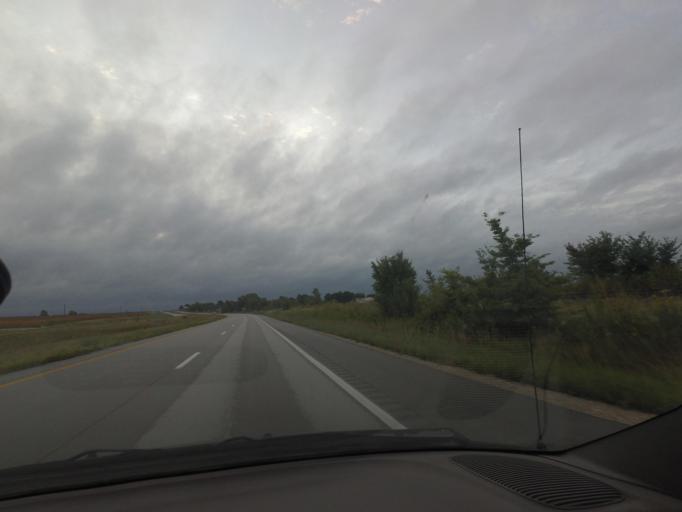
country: US
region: Missouri
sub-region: Shelby County
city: Shelbina
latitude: 39.6752
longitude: -91.9607
